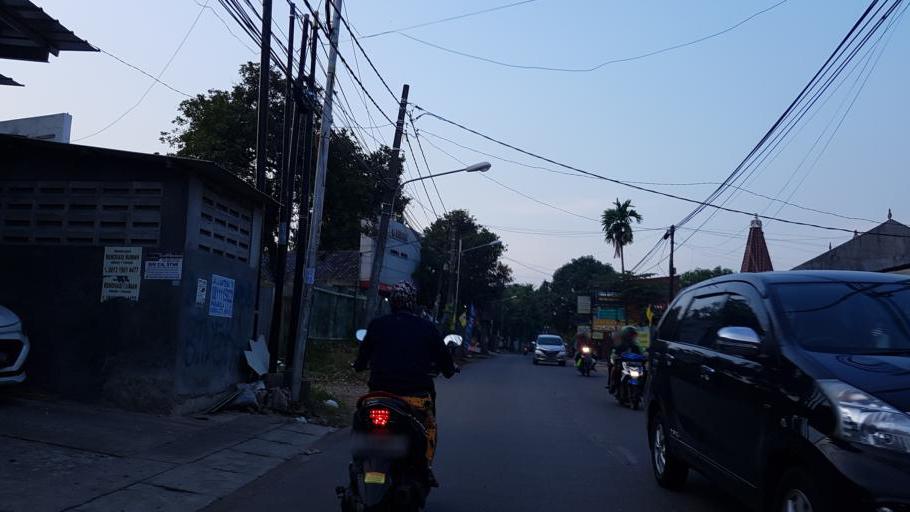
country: ID
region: West Java
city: Bekasi
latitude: -6.2704
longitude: 106.9503
